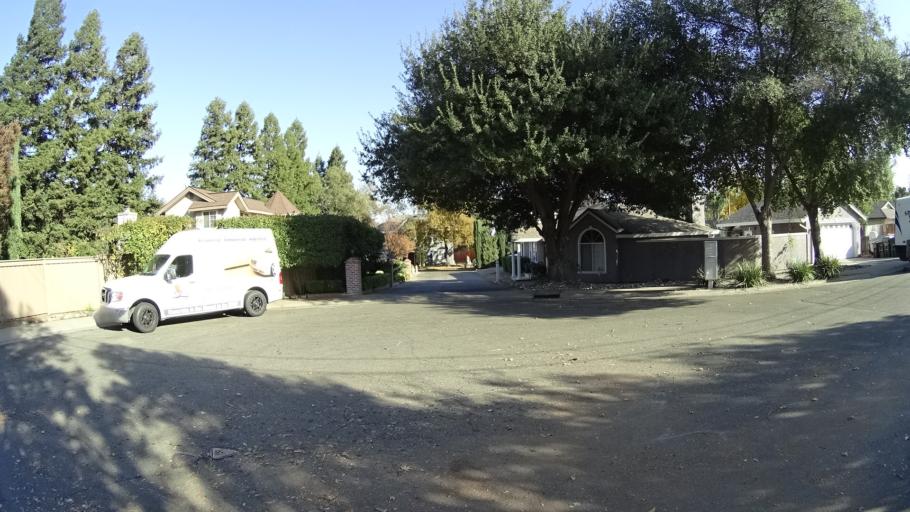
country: US
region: California
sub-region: Sacramento County
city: Citrus Heights
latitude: 38.6766
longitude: -121.2877
